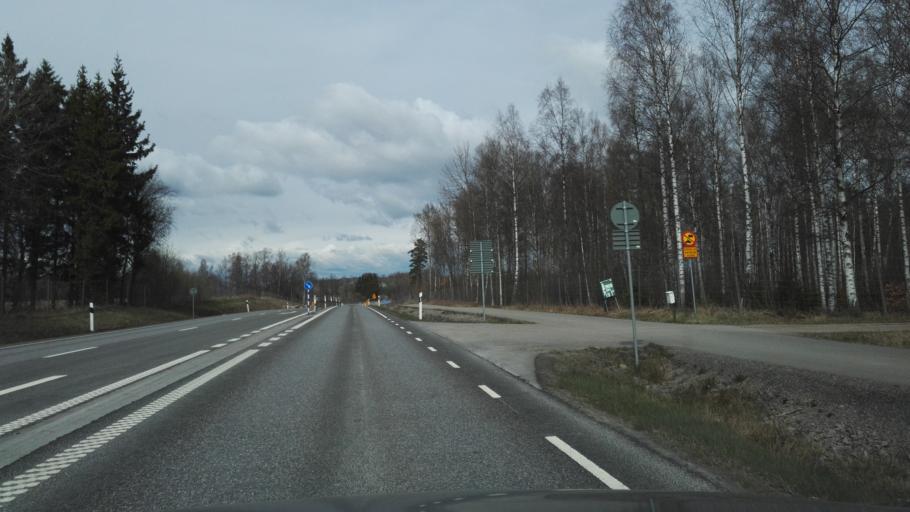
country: SE
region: Kronoberg
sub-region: Vaxjo Kommun
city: Vaexjoe
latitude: 56.9336
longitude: 14.8667
